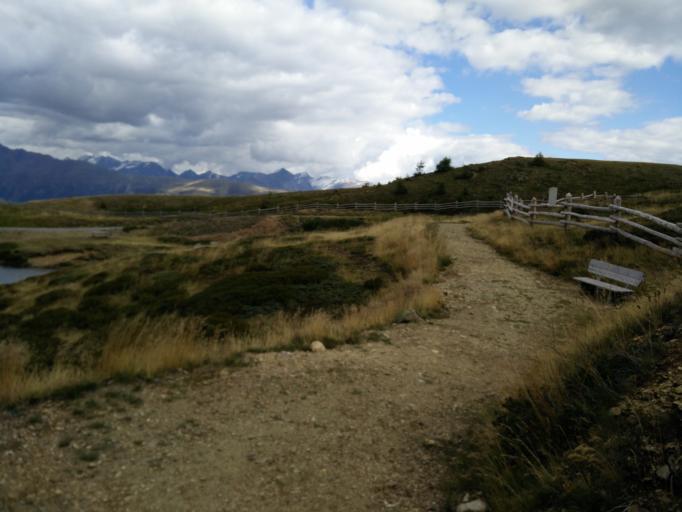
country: IT
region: Trentino-Alto Adige
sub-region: Bolzano
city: Malles Venosta
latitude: 46.7158
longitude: 10.4954
